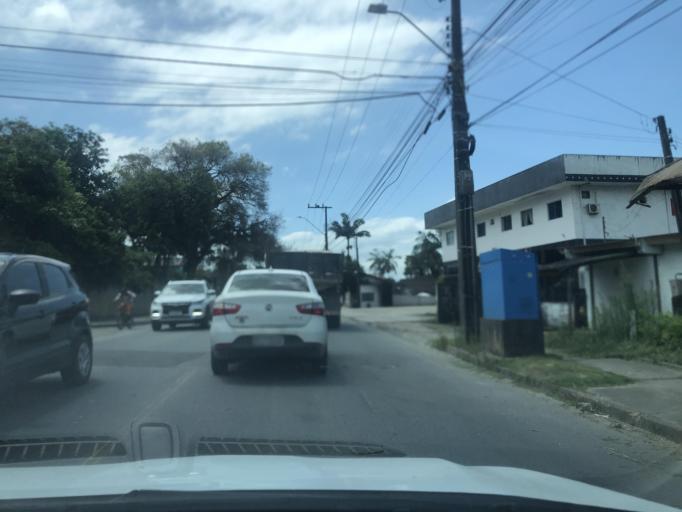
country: BR
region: Santa Catarina
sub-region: Joinville
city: Joinville
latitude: -26.3414
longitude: -48.7977
